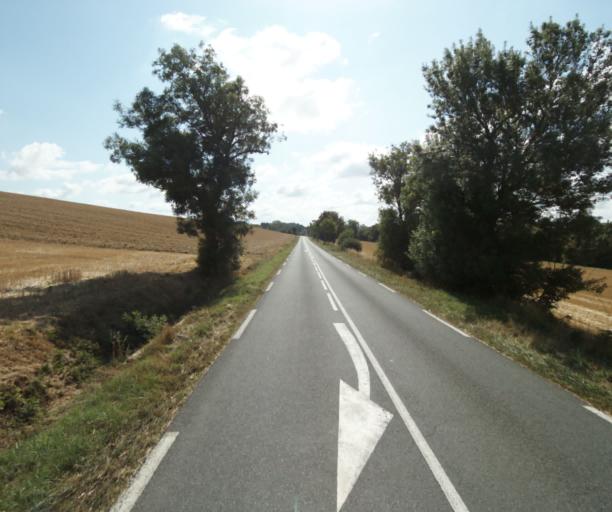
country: FR
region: Midi-Pyrenees
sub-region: Departement de la Haute-Garonne
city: Avignonet-Lauragais
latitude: 43.4457
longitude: 1.8027
